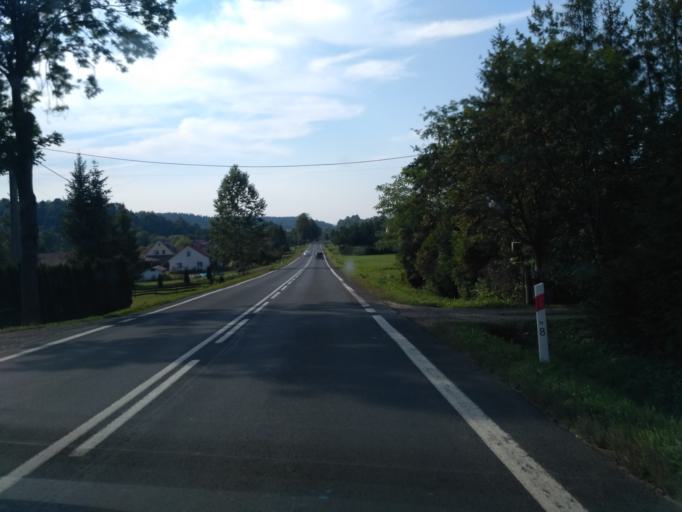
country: PL
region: Subcarpathian Voivodeship
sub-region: Powiat leski
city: Olszanica
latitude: 49.4377
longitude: 22.4993
